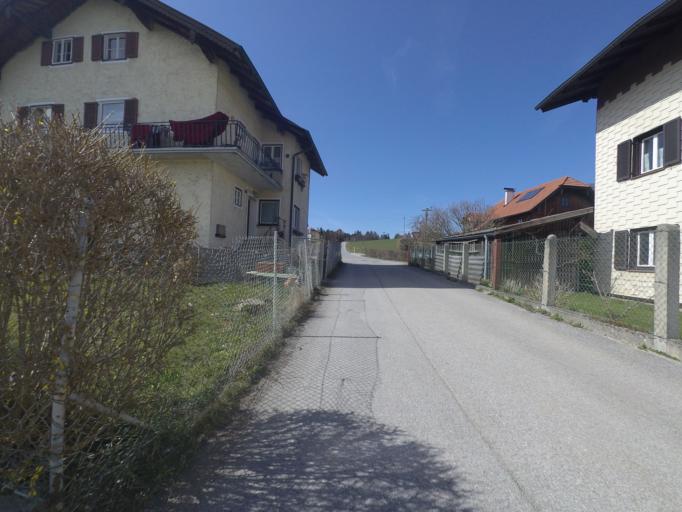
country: AT
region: Salzburg
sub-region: Politischer Bezirk Salzburg-Umgebung
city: Seekirchen am Wallersee
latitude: 47.8974
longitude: 13.1135
